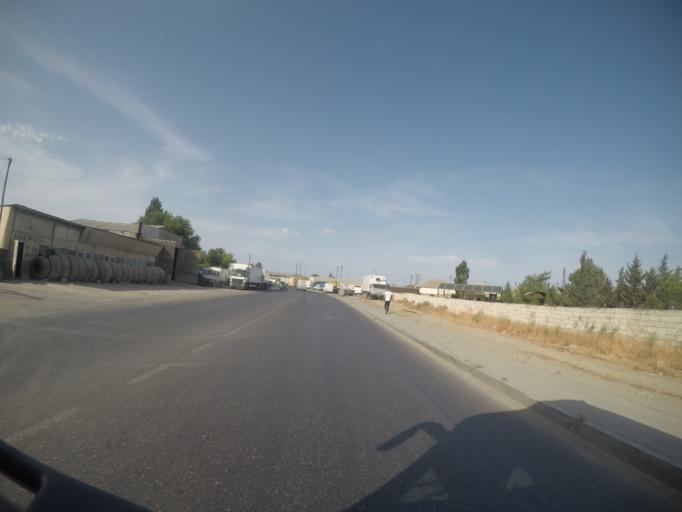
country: AZ
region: Baki
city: Bilajari
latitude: 40.4405
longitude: 49.7844
